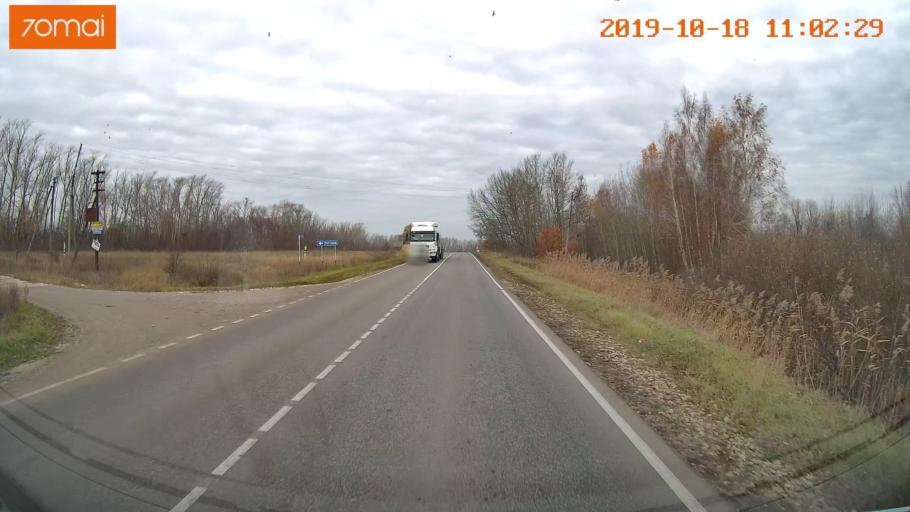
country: RU
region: Tula
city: Yepifan'
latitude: 53.8663
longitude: 38.5444
